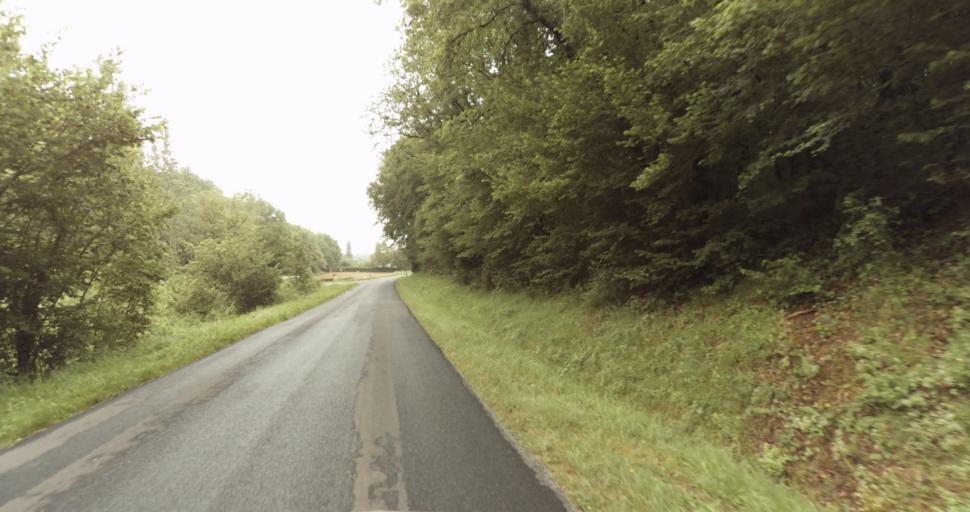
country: FR
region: Aquitaine
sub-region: Departement de la Dordogne
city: Lalinde
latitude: 44.8731
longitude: 0.7732
